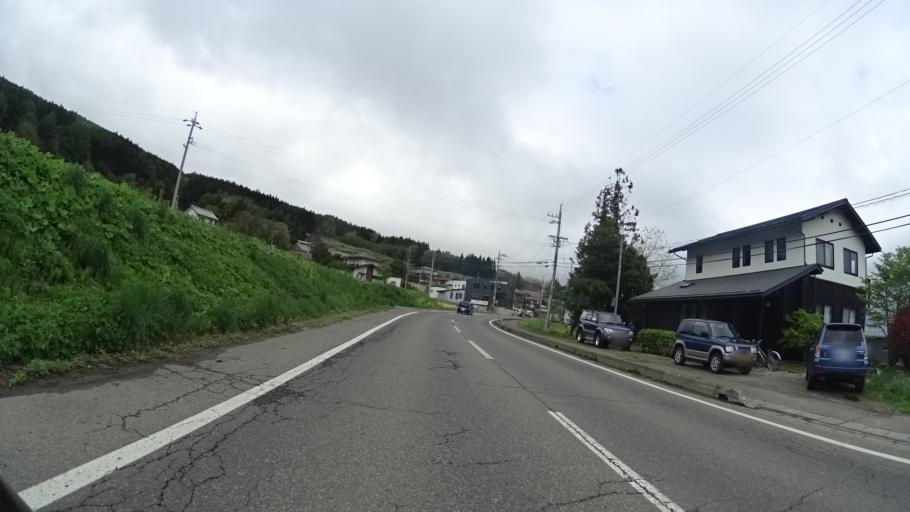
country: JP
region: Nagano
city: Nagano-shi
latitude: 36.7377
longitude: 138.2054
